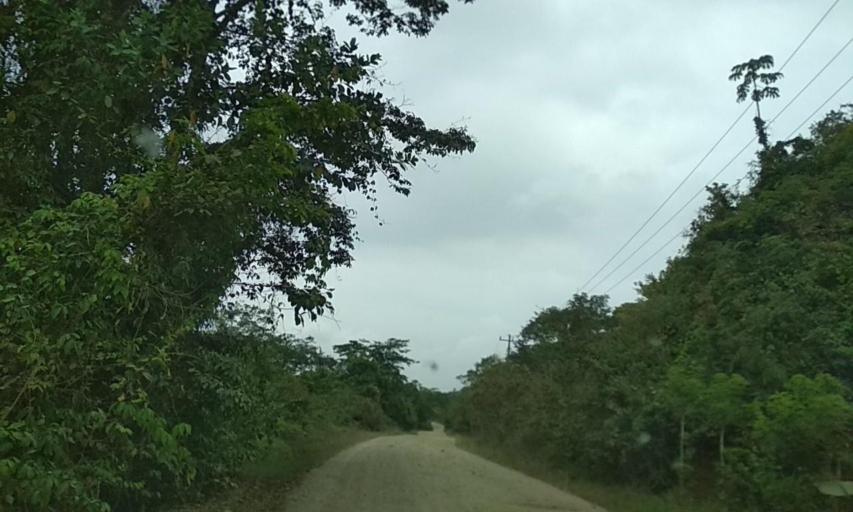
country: MX
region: Veracruz
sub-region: Uxpanapa
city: Poblado 10
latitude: 17.4538
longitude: -94.0896
